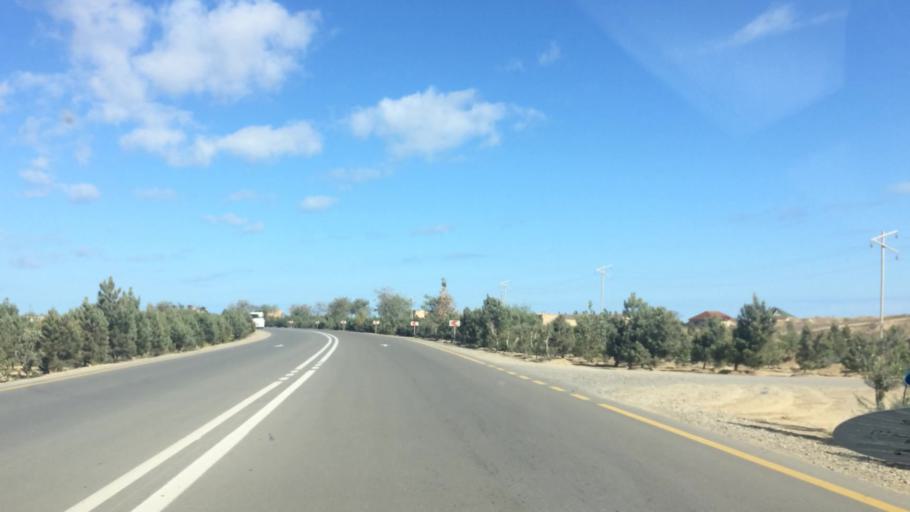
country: AZ
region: Baki
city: Pirallahi
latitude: 40.4219
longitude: 50.3563
